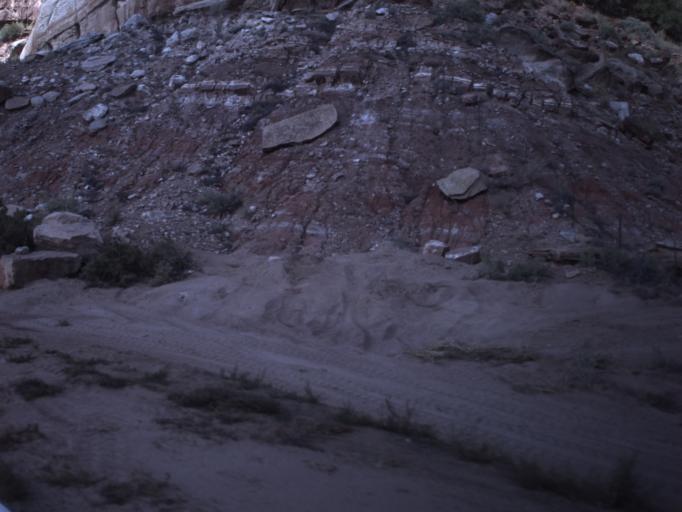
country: US
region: Utah
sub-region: San Juan County
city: Blanding
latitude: 37.2860
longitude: -109.5216
